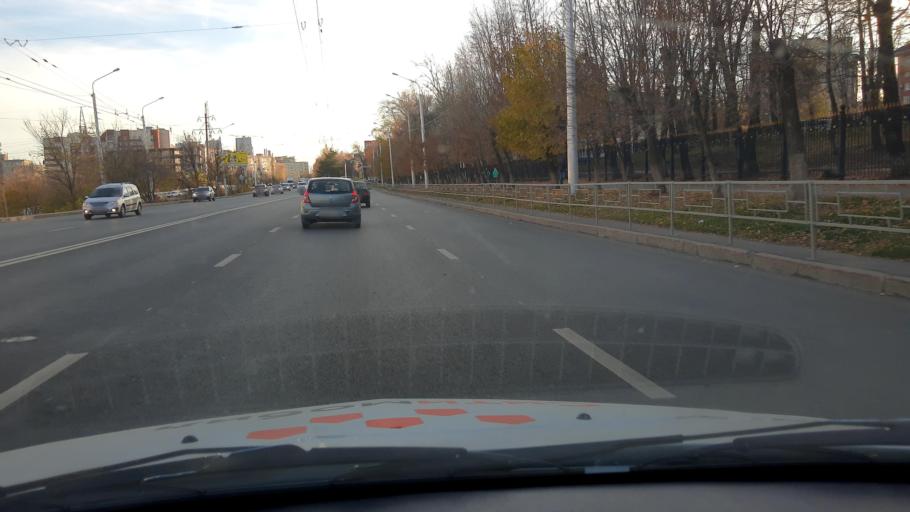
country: RU
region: Bashkortostan
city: Ufa
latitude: 54.7754
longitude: 56.0344
